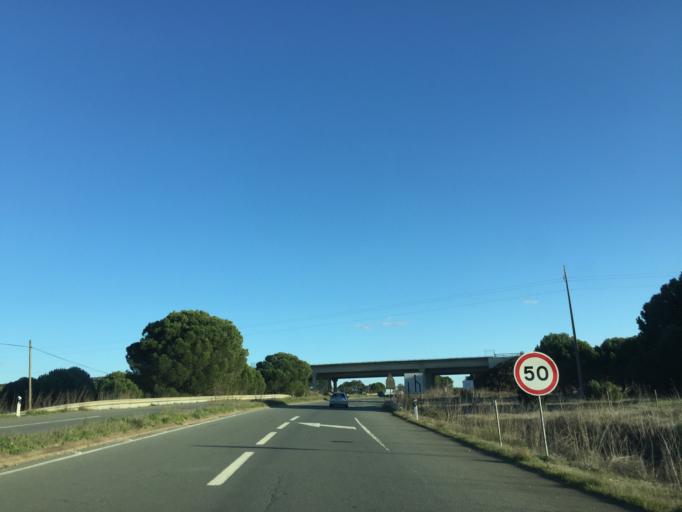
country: PT
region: Setubal
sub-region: Grandola
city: Grandola
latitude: 38.1180
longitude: -8.4214
